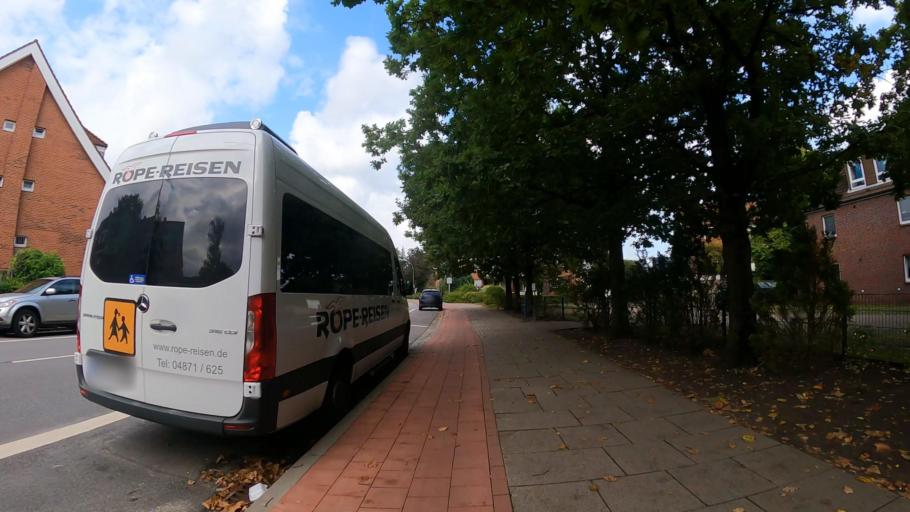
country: DE
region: Schleswig-Holstein
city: Elmshorn
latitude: 53.7370
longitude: 9.6701
